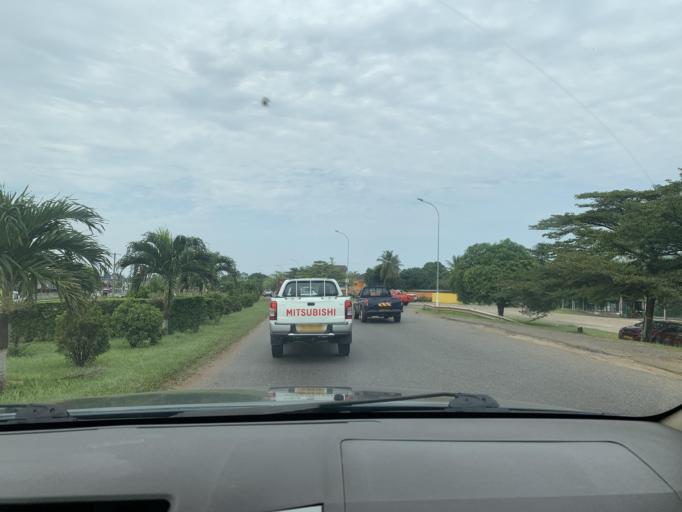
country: GA
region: Estuaire
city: Libreville
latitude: 0.3407
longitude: 9.4768
